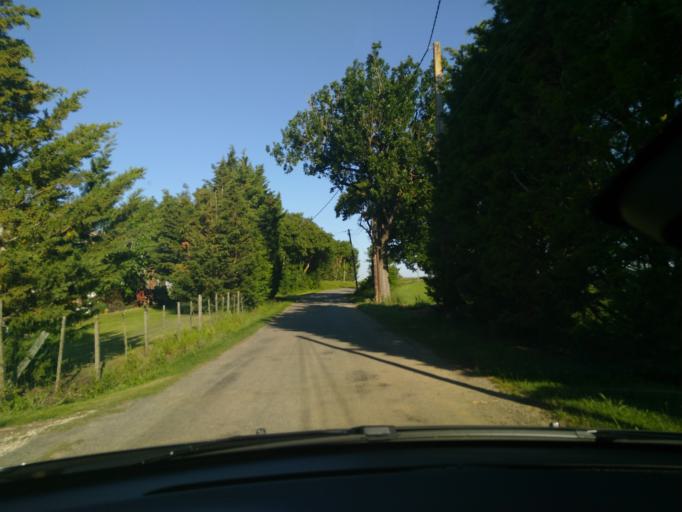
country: FR
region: Midi-Pyrenees
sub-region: Departement du Tarn-et-Garonne
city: Beaumont-de-Lomagne
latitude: 43.7822
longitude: 0.9753
